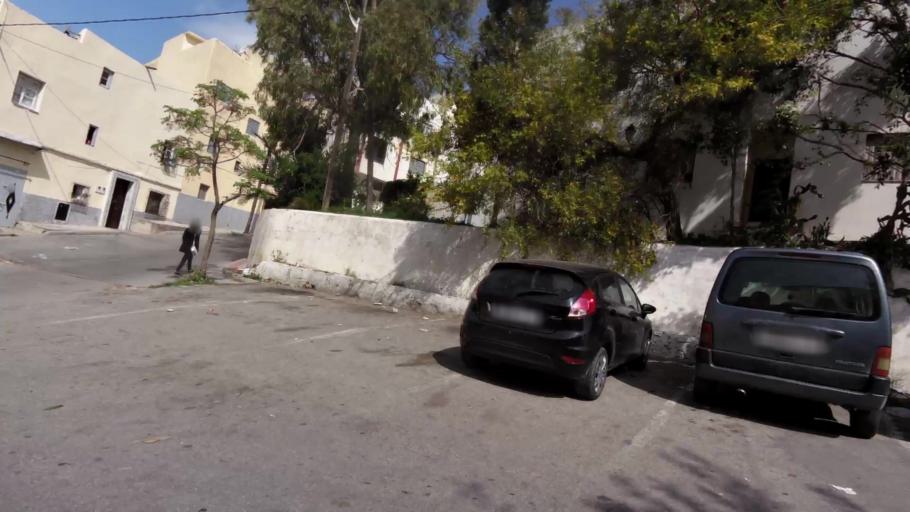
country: MA
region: Tanger-Tetouan
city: Tetouan
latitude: 35.5767
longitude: -5.3862
